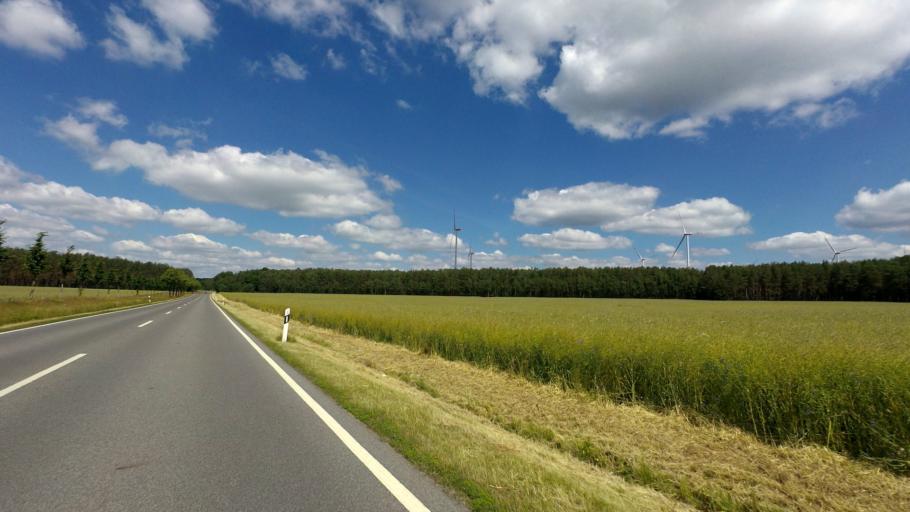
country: DE
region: Brandenburg
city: Sallgast
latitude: 51.6205
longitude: 13.7937
